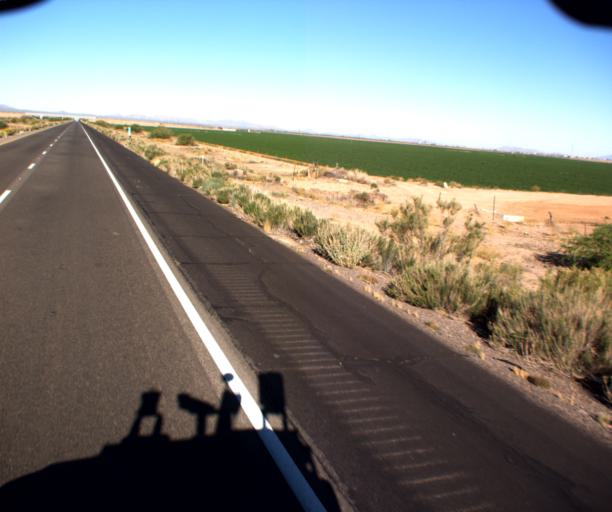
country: US
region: Arizona
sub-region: Pinal County
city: Casa Grande
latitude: 32.8283
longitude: -111.9029
